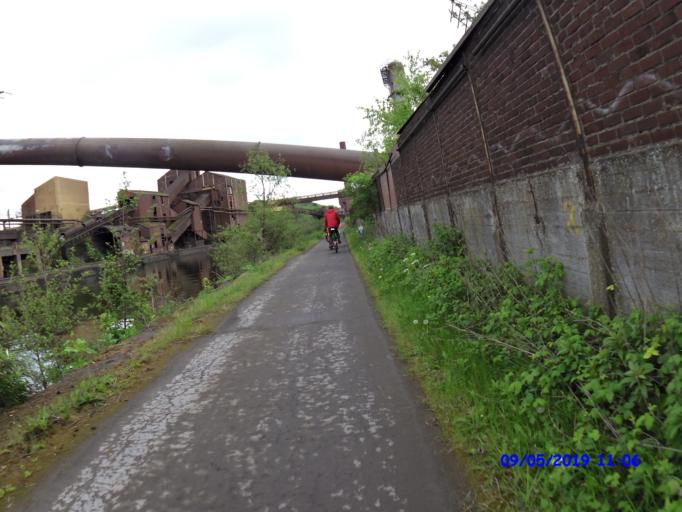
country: BE
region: Wallonia
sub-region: Province du Hainaut
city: Charleroi
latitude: 50.4113
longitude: 4.4178
